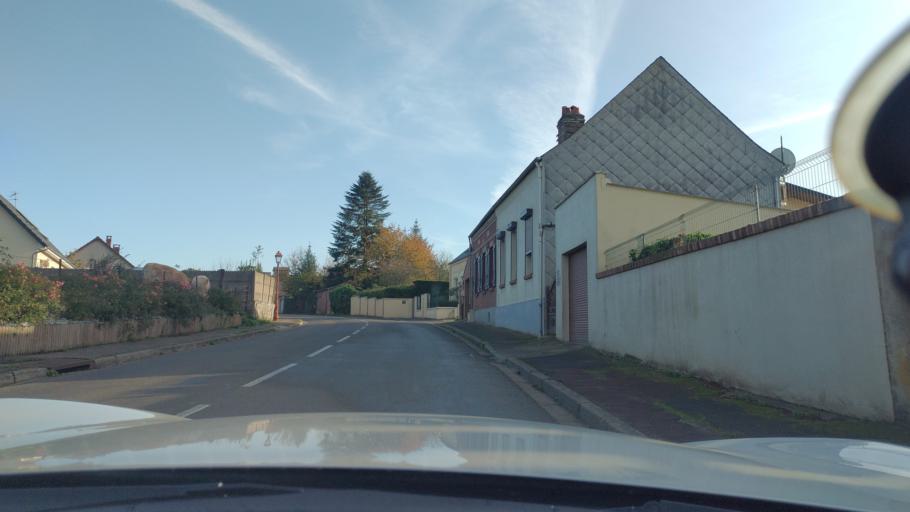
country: FR
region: Picardie
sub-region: Departement de la Somme
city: Fressenneville
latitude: 50.0690
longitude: 1.5683
